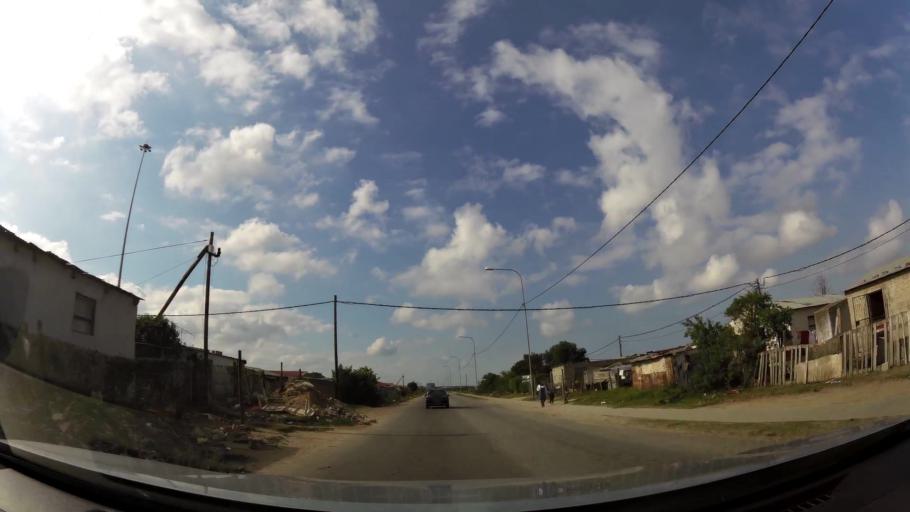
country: ZA
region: Eastern Cape
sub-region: Nelson Mandela Bay Metropolitan Municipality
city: Port Elizabeth
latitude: -33.7869
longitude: 25.5886
